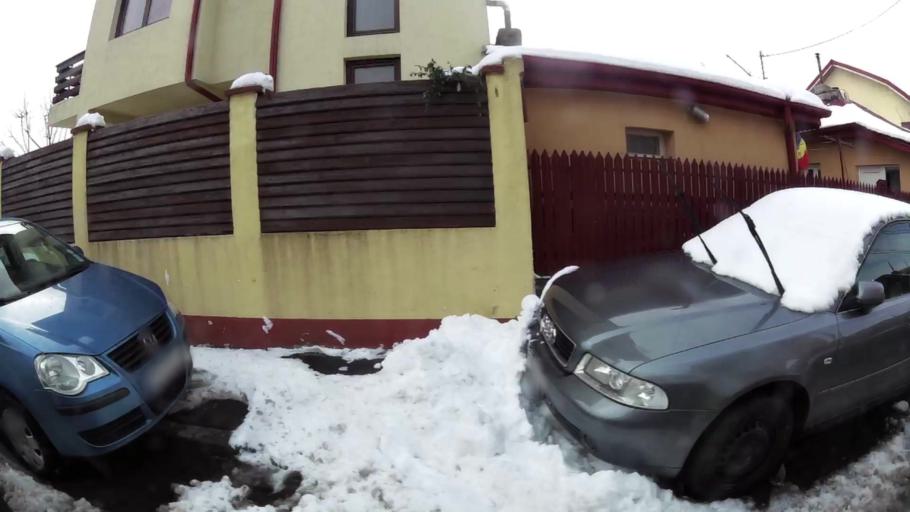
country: RO
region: Bucuresti
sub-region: Municipiul Bucuresti
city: Bucuresti
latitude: 44.3864
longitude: 26.1129
